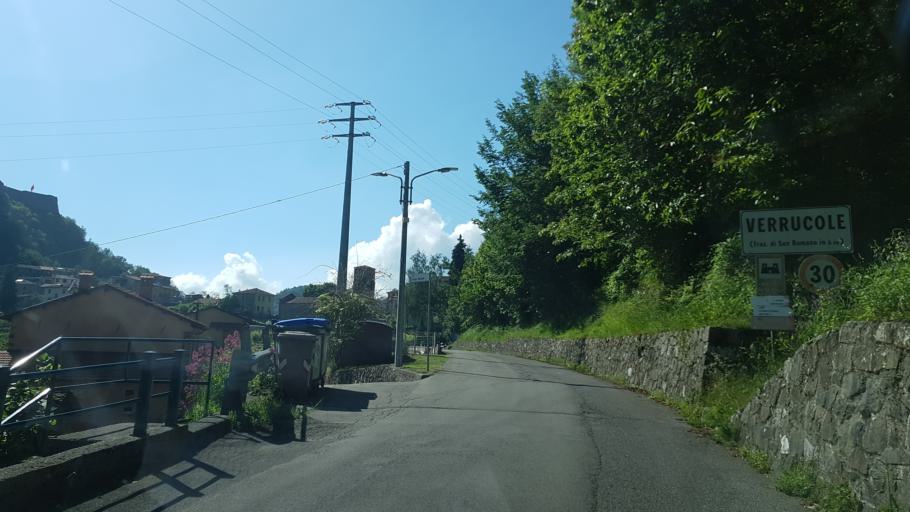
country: IT
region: Tuscany
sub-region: Provincia di Lucca
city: San Romano
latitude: 44.1791
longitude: 10.3381
